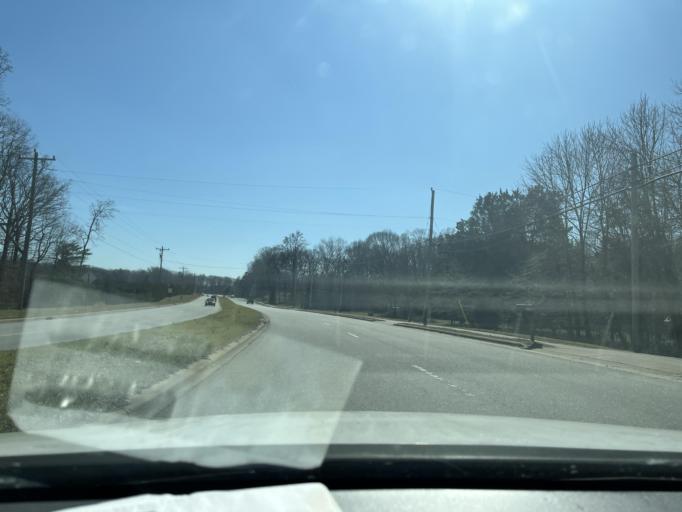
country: US
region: North Carolina
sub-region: Guilford County
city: Jamestown
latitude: 36.0204
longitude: -79.9269
